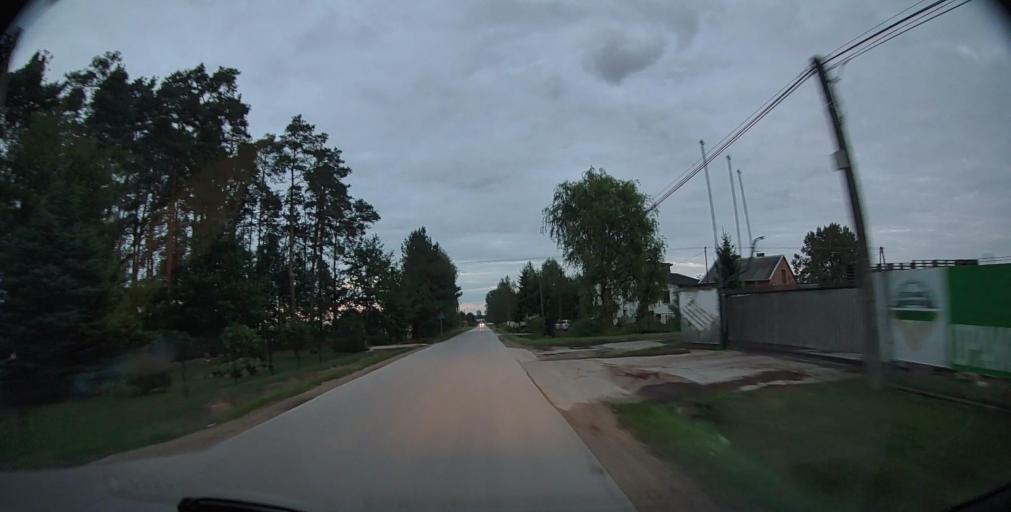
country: PL
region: Masovian Voivodeship
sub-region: Powiat radomski
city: Jedlinsk
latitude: 51.4653
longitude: 21.1282
